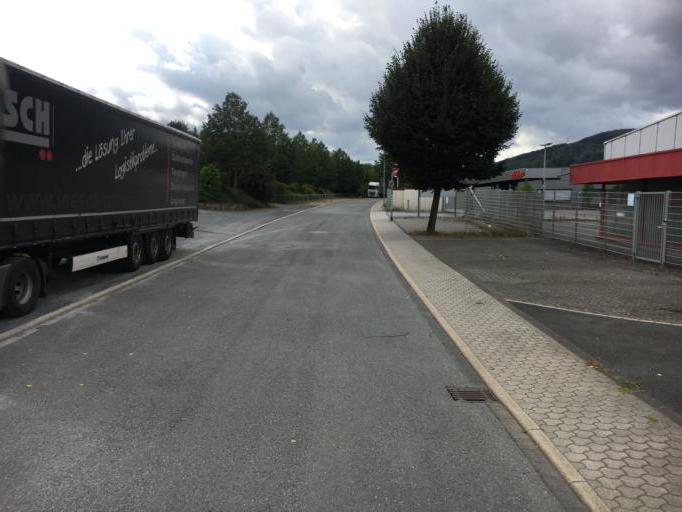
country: DE
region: North Rhine-Westphalia
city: Plettenberg
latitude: 51.1964
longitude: 7.8418
